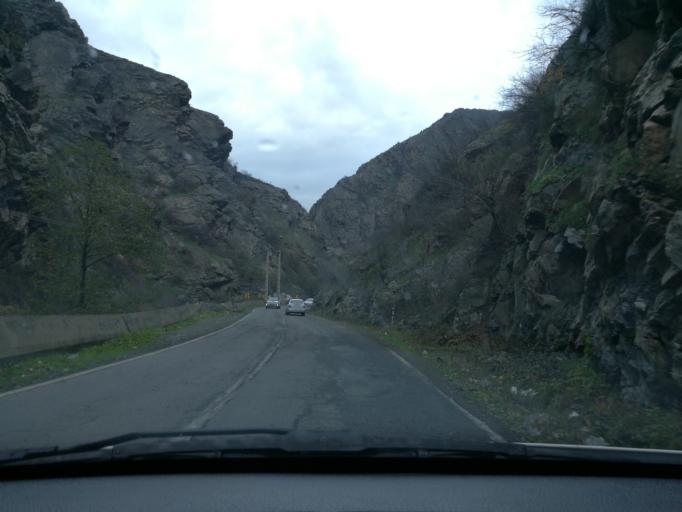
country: IR
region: Mazandaran
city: Chalus
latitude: 36.2984
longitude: 51.2472
